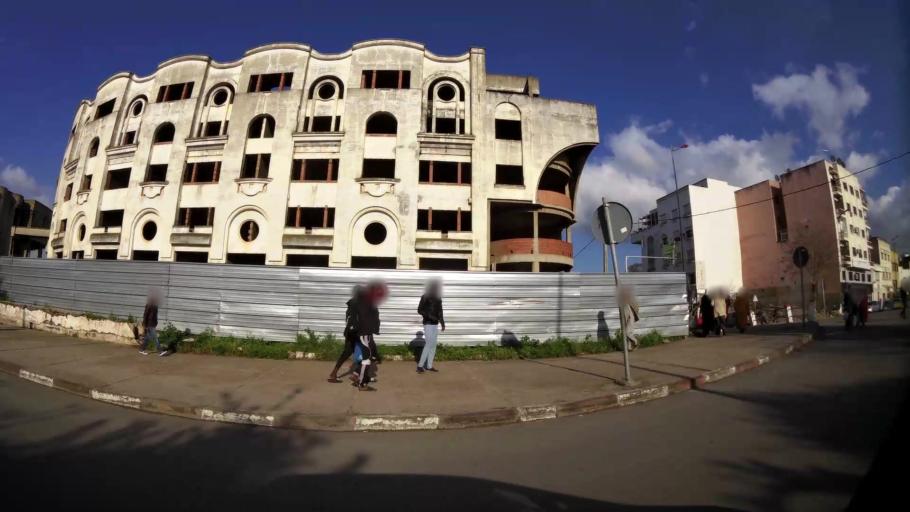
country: MA
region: Chaouia-Ouardigha
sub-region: Settat Province
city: Settat
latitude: 33.0025
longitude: -7.6221
